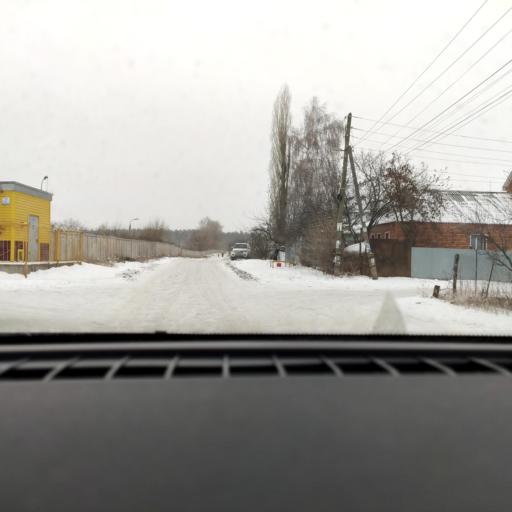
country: RU
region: Voronezj
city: Maslovka
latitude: 51.6091
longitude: 39.2246
